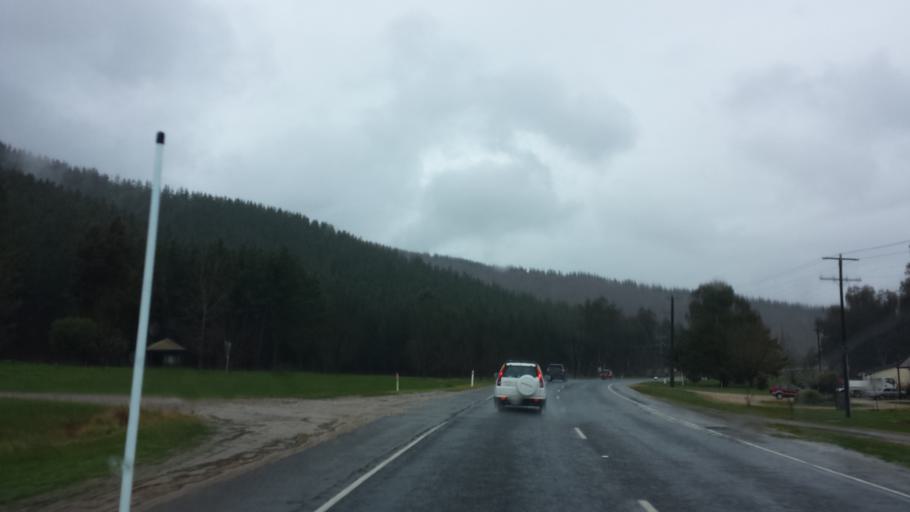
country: AU
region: Victoria
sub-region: Alpine
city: Mount Beauty
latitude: -36.5739
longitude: 146.7446
